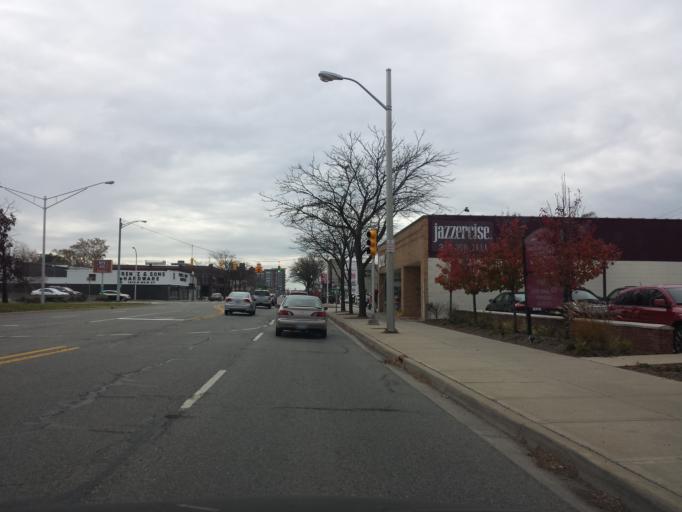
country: US
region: Michigan
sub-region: Oakland County
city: Royal Oak
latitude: 42.4992
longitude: -83.1449
